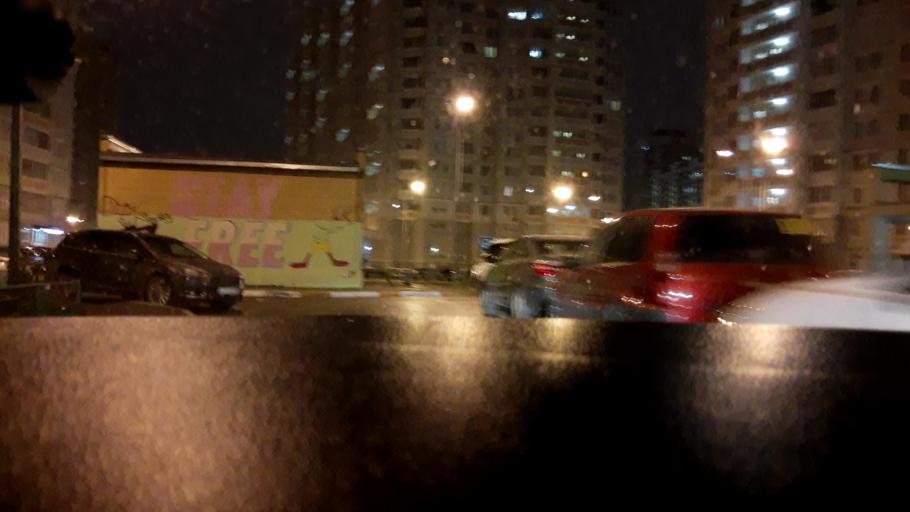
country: RU
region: Moskovskaya
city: Zheleznodorozhnyy
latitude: 55.7442
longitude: 37.9962
